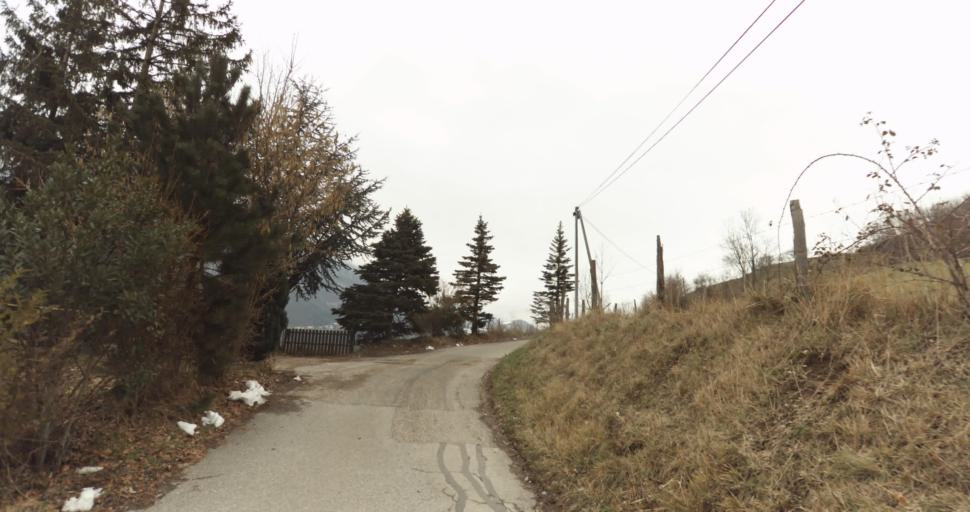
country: FR
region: Rhone-Alpes
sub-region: Departement de l'Isere
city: Saint-Georges-de-Commiers
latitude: 45.0243
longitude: 5.6891
